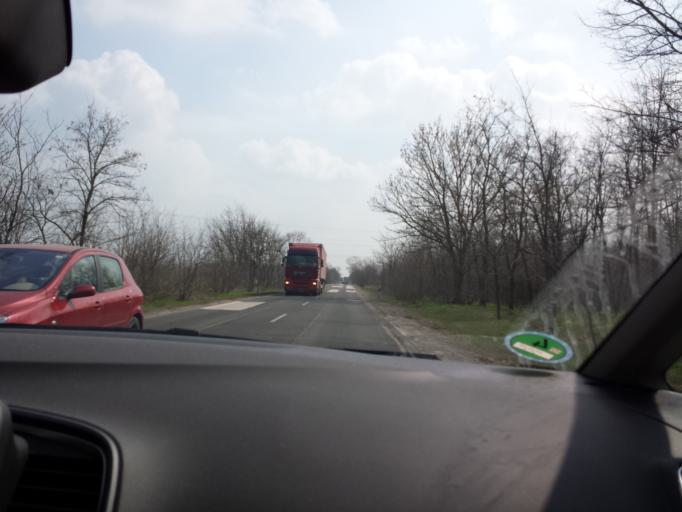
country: HU
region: Bacs-Kiskun
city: Nyarlorinc
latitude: 46.8825
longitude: 19.8419
